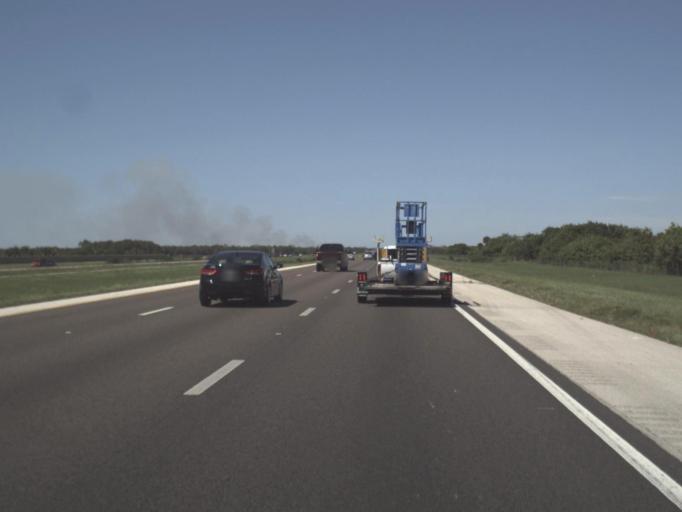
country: US
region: Florida
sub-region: Lee County
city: Bonita Springs
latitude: 26.3585
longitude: -81.7595
